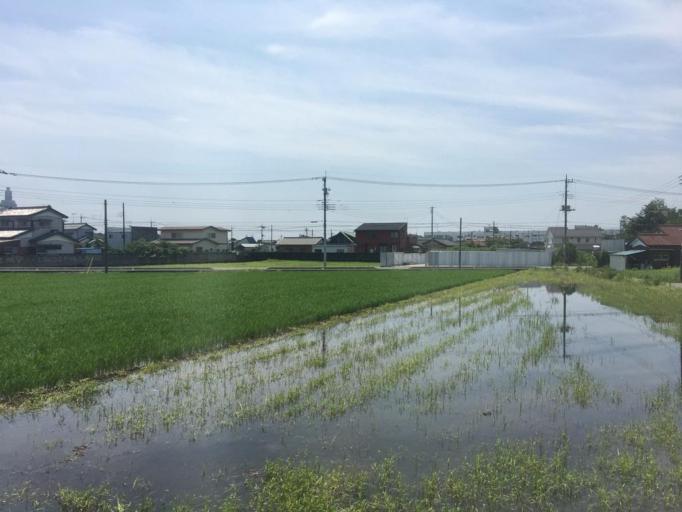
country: JP
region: Gunma
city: Tatebayashi
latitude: 36.2575
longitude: 139.4584
